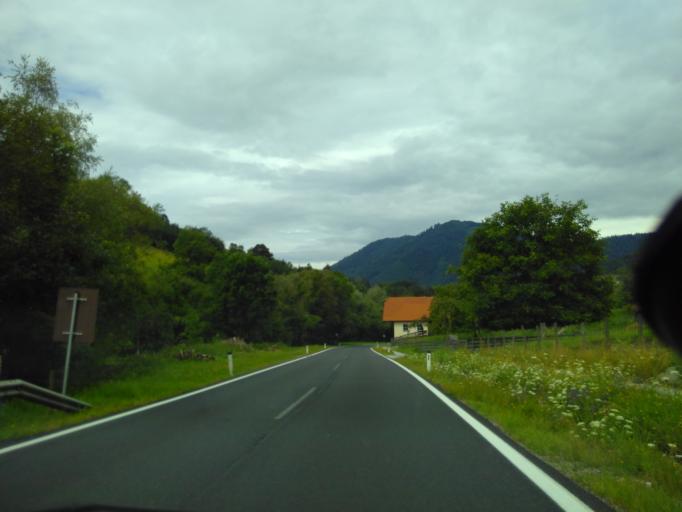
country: AT
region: Styria
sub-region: Politischer Bezirk Graz-Umgebung
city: Schrems bei Frohnleiten
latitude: 47.2761
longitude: 15.3815
